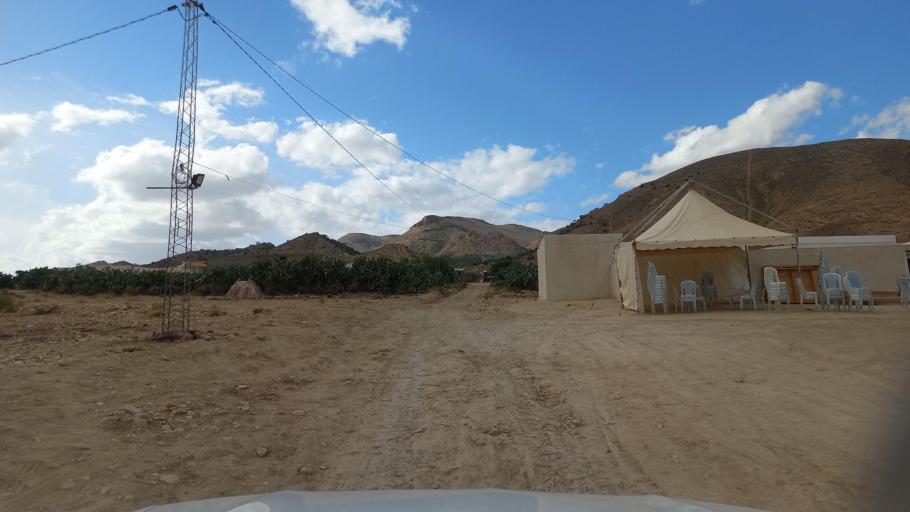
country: TN
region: Al Qasrayn
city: Sbiba
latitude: 35.4511
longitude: 9.0651
